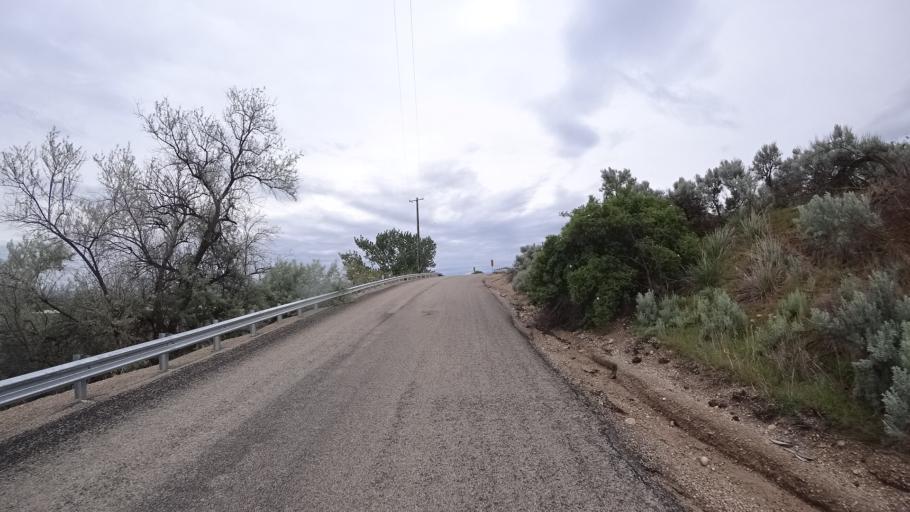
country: US
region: Idaho
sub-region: Ada County
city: Star
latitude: 43.6693
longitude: -116.4728
